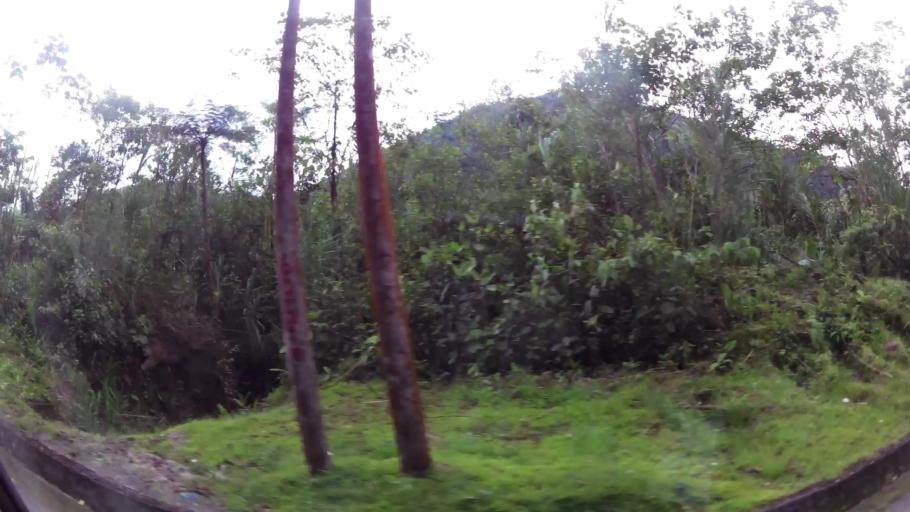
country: EC
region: Pastaza
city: Puyo
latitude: -1.4281
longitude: -78.1770
